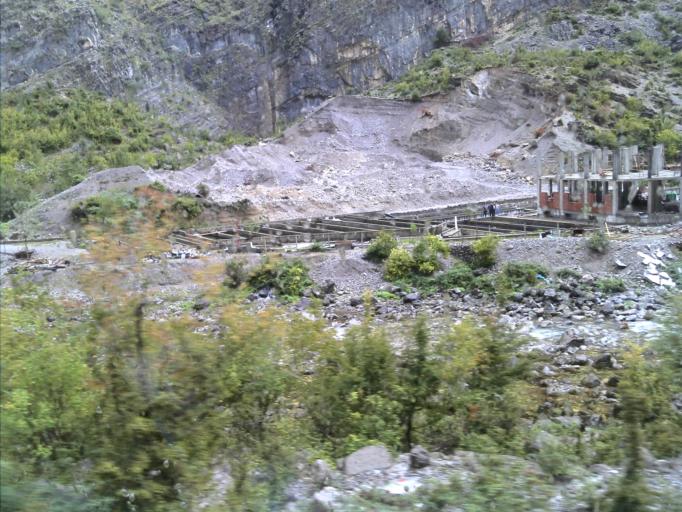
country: AL
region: Shkoder
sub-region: Rrethi i Malesia e Madhe
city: Kastrat
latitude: 42.4818
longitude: 19.5821
